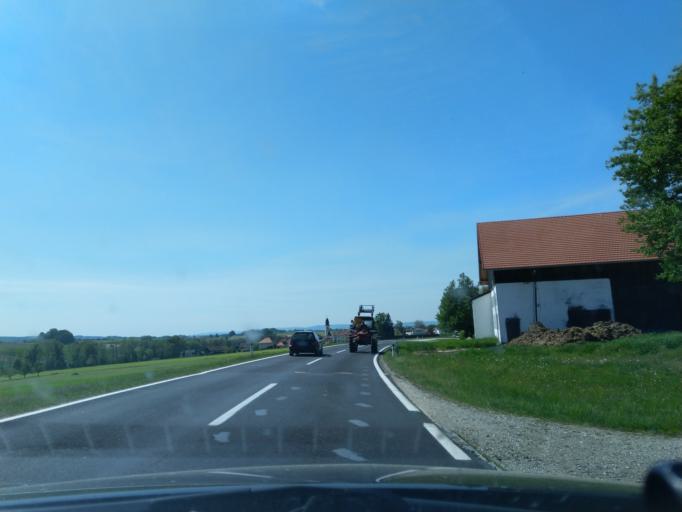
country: DE
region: Bavaria
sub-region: Lower Bavaria
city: Bad Fussing
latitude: 48.2757
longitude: 13.3814
